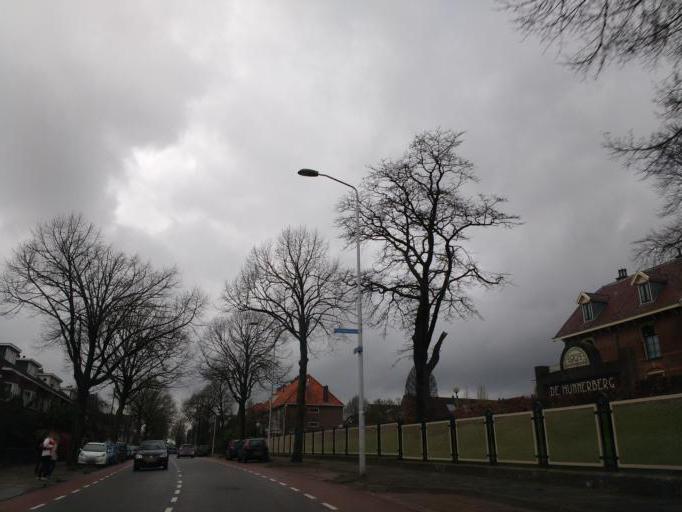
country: NL
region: Gelderland
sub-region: Gemeente Groesbeek
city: Berg en Dal
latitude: 51.8352
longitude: 5.8892
